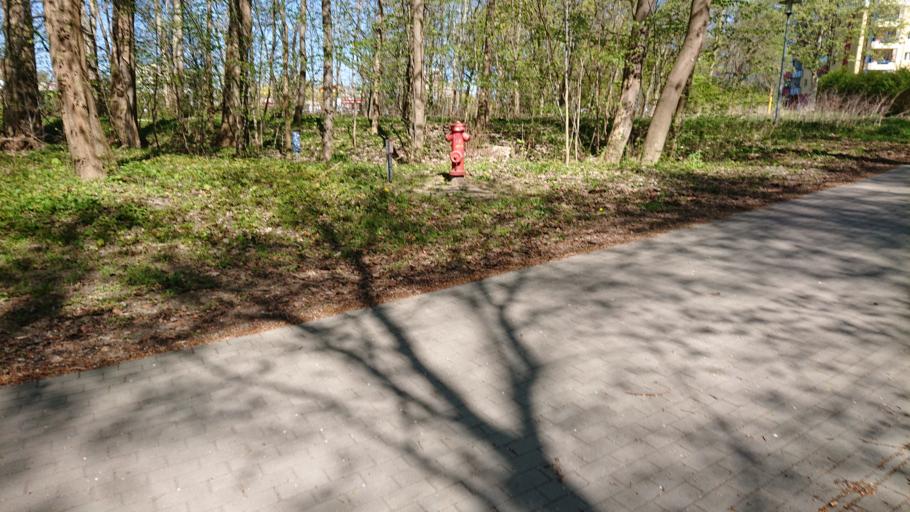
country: DE
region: Mecklenburg-Vorpommern
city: Stralsund
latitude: 54.3195
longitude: 13.0564
